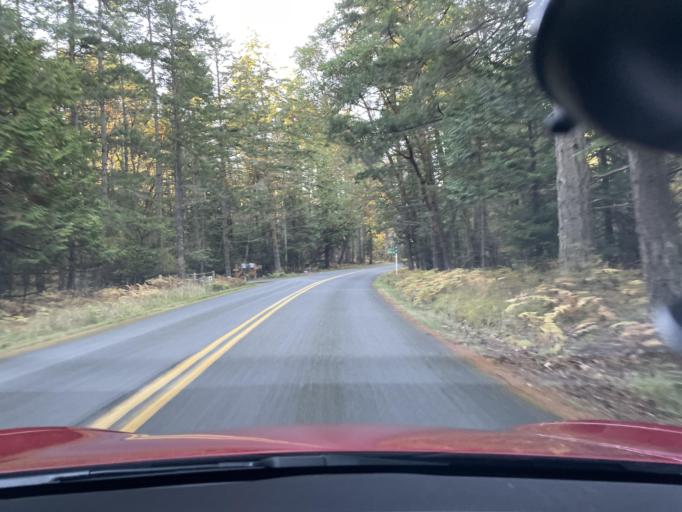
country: US
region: Washington
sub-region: San Juan County
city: Friday Harbor
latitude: 48.5343
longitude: -123.1594
